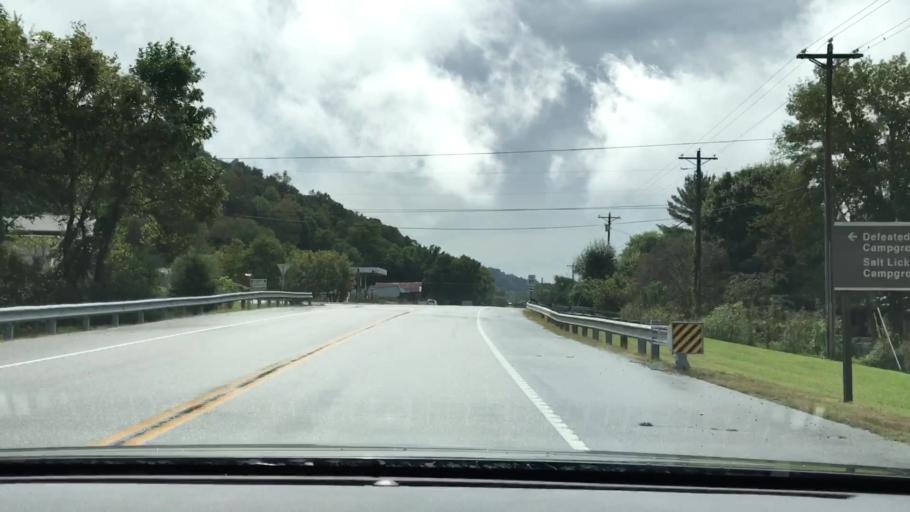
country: US
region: Tennessee
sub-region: Smith County
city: Carthage
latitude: 36.3192
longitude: -85.9688
